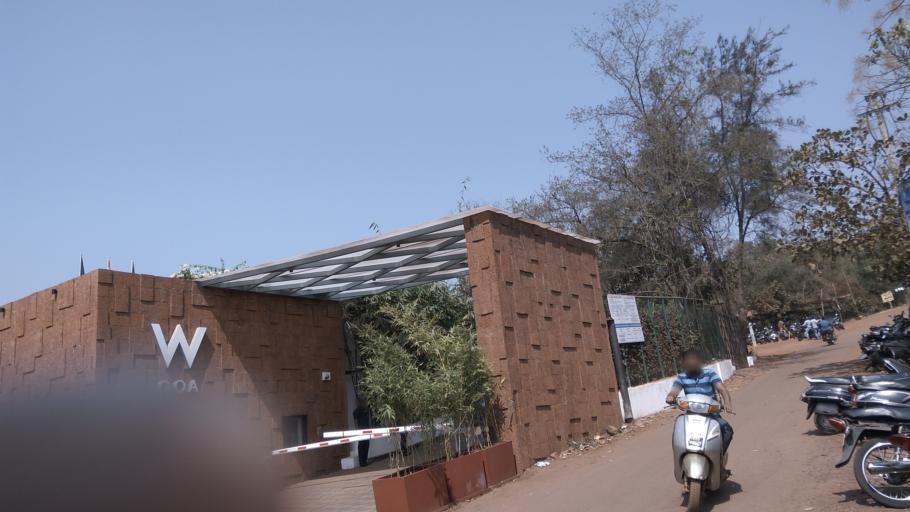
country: IN
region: Goa
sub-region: North Goa
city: Vagator
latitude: 15.6023
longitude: 73.7371
